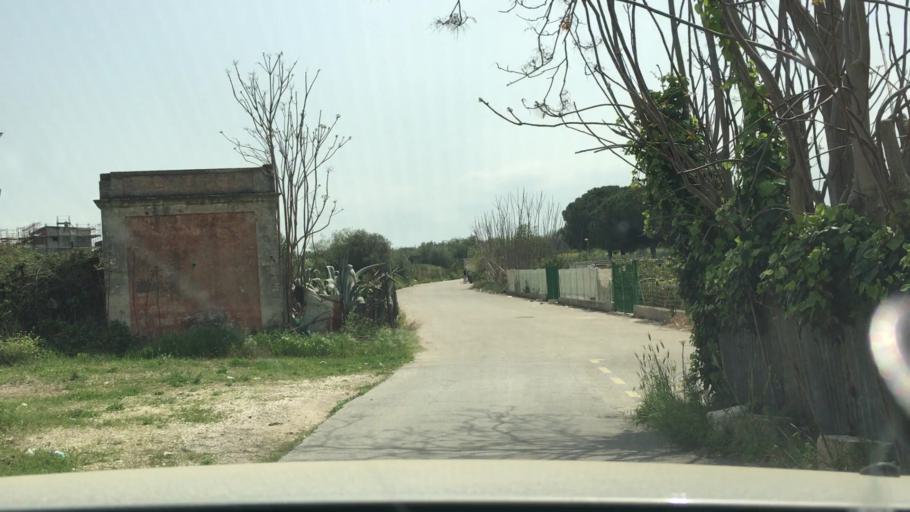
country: IT
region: Apulia
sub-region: Provincia di Barletta - Andria - Trani
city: Capirro
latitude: 41.2588
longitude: 16.4527
